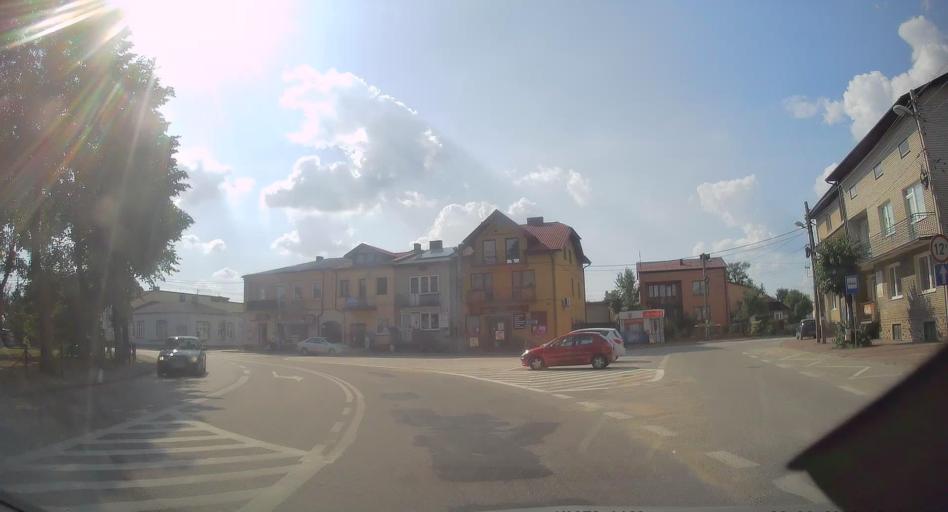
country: PL
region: Swietokrzyskie
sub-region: Powiat konecki
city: Radoszyce
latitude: 51.0740
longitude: 20.2596
